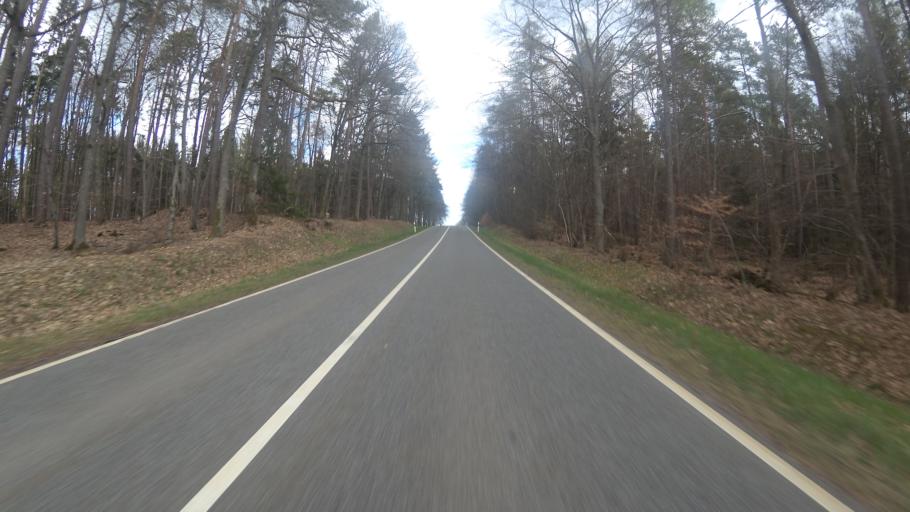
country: DE
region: Rheinland-Pfalz
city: Greimerath
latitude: 50.0317
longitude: 6.9046
